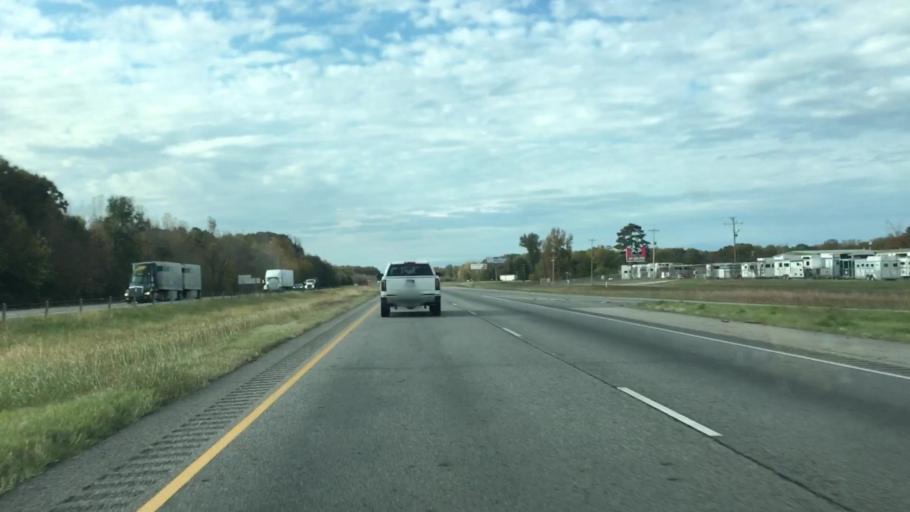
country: US
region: Arkansas
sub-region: Pope County
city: Atkins
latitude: 35.2214
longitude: -92.8325
